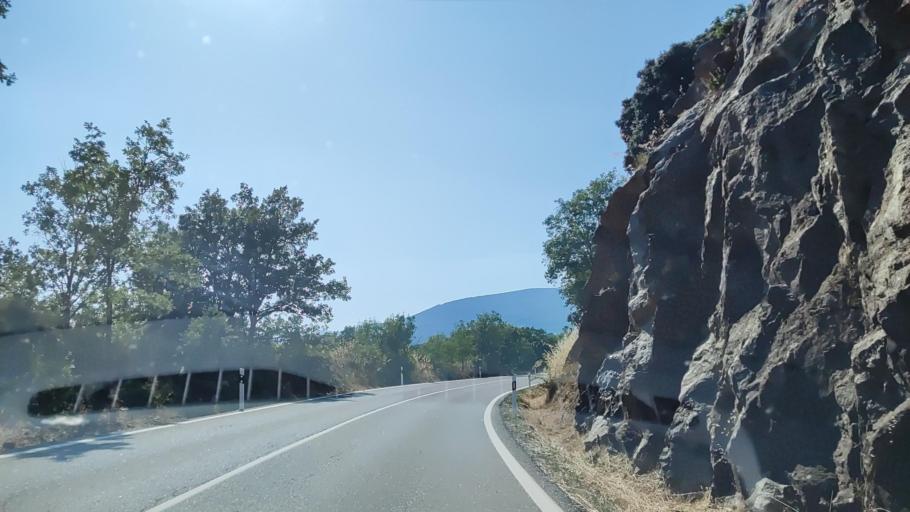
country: ES
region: Madrid
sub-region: Provincia de Madrid
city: Lozoya
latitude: 40.9481
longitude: -3.7671
